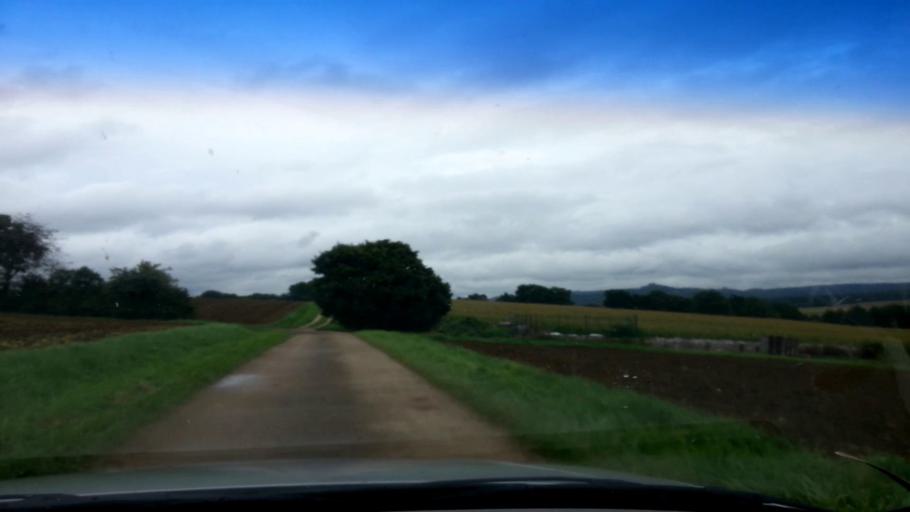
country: DE
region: Bavaria
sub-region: Upper Franconia
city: Memmelsdorf
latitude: 49.9472
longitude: 10.9808
